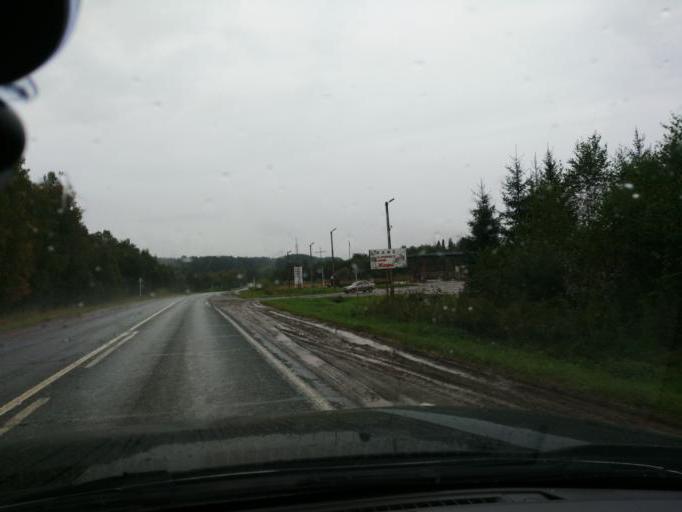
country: RU
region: Perm
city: Yugo-Kamskiy
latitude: 57.5399
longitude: 55.6866
